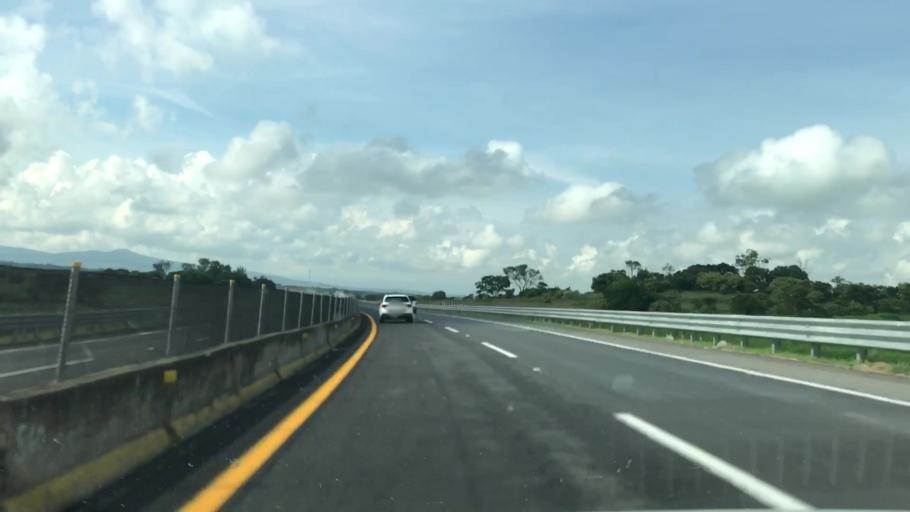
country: MX
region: Jalisco
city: Zapotlanejo
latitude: 20.6318
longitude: -103.0919
